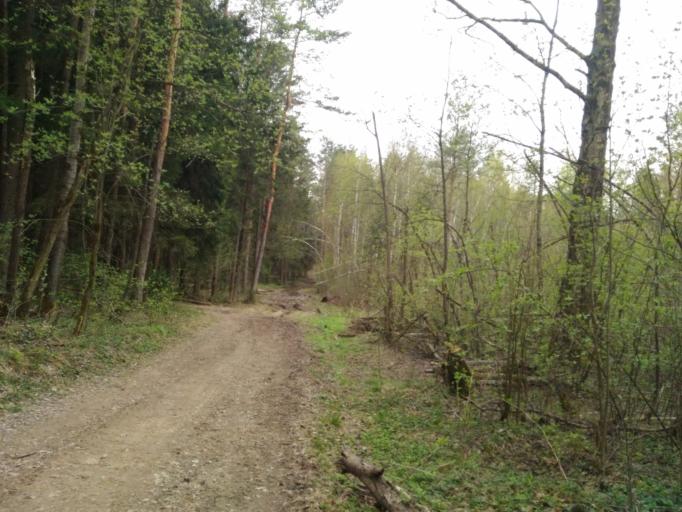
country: RU
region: Moskovskaya
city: Dedovsk
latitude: 55.8443
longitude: 37.1100
